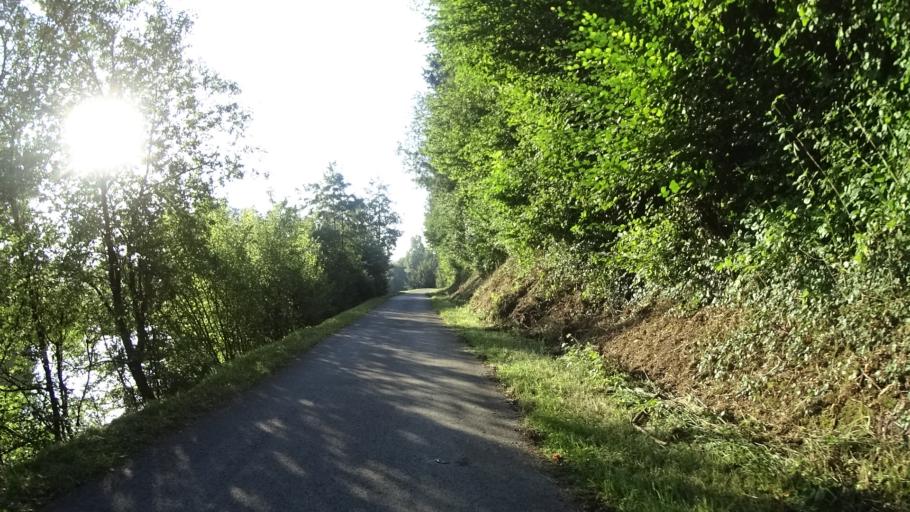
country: FR
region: Franche-Comte
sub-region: Territoire de Belfort
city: Mezire
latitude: 47.5403
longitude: 6.9087
